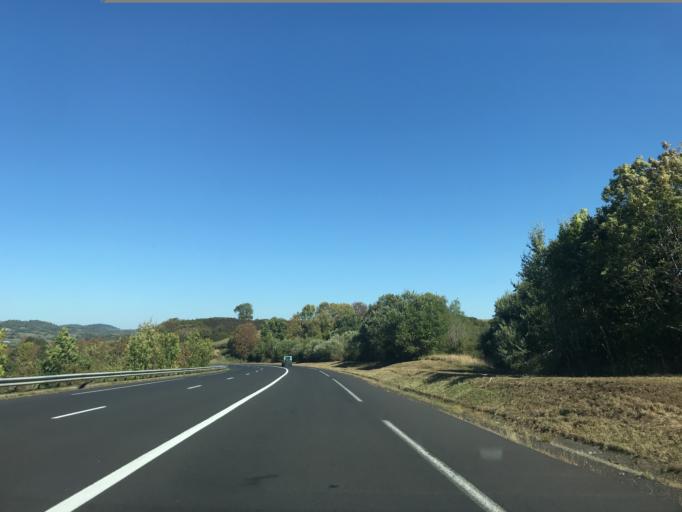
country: FR
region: Auvergne
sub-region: Departement du Puy-de-Dome
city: Gelles
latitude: 45.7159
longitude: 2.8061
